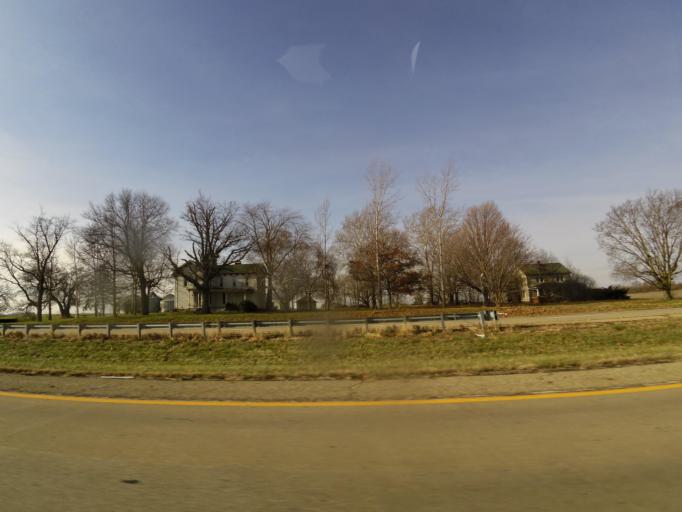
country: US
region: Illinois
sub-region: Macon County
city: Forsyth
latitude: 39.9831
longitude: -88.9560
